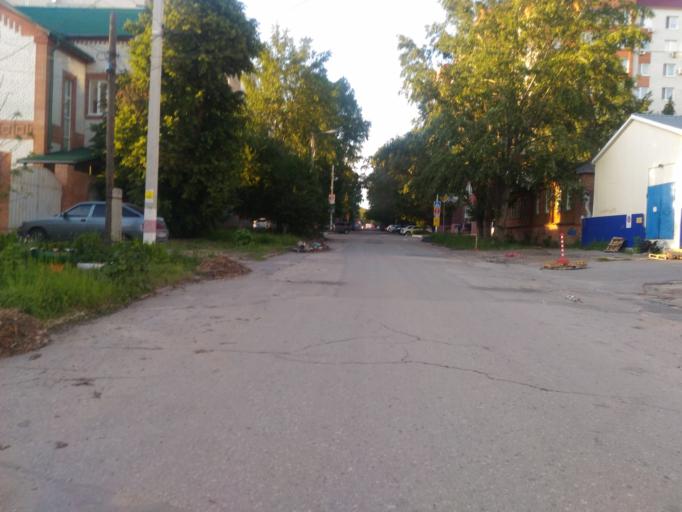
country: RU
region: Ulyanovsk
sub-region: Ulyanovskiy Rayon
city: Ulyanovsk
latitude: 54.3203
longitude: 48.3815
